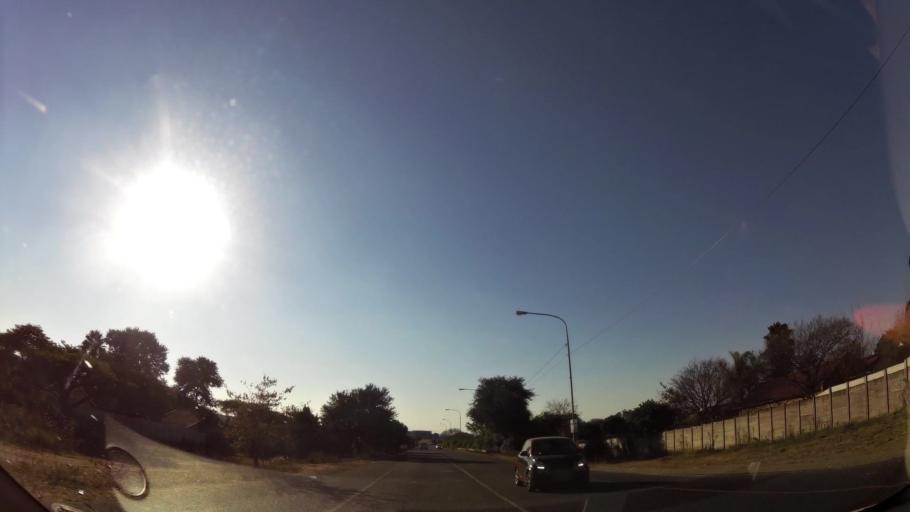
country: ZA
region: Gauteng
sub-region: City of Tshwane Metropolitan Municipality
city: Centurion
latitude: -25.8904
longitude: 28.1428
